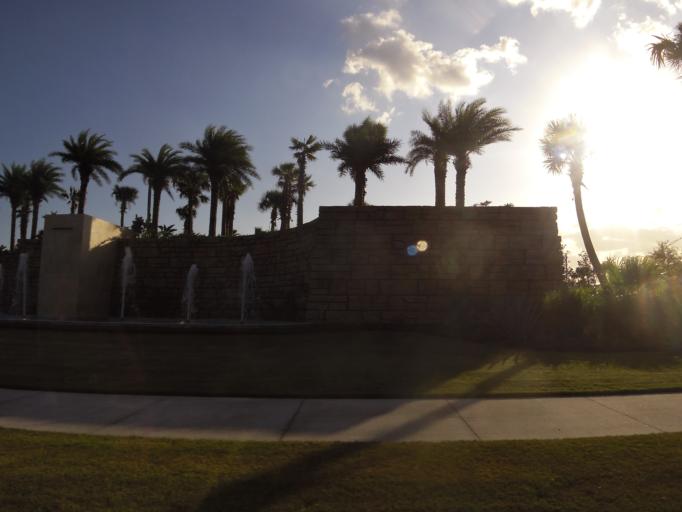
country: US
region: Florida
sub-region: Saint Johns County
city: Palm Valley
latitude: 30.0771
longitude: -81.4845
